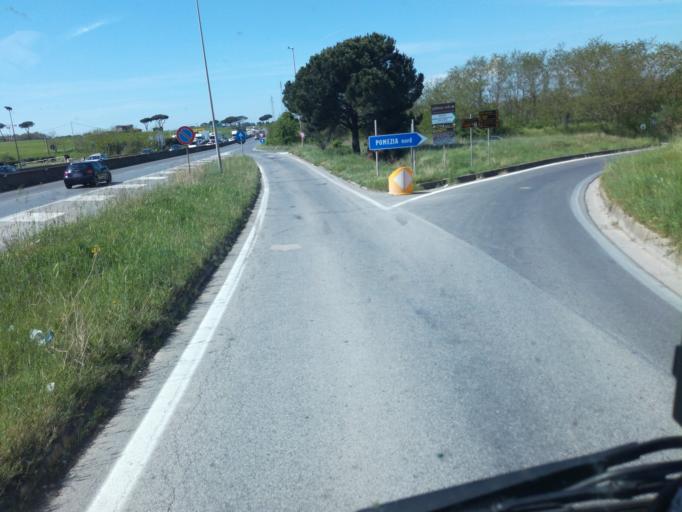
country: IT
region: Latium
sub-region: Citta metropolitana di Roma Capitale
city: Area Produttiva
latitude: 41.6906
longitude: 12.4832
